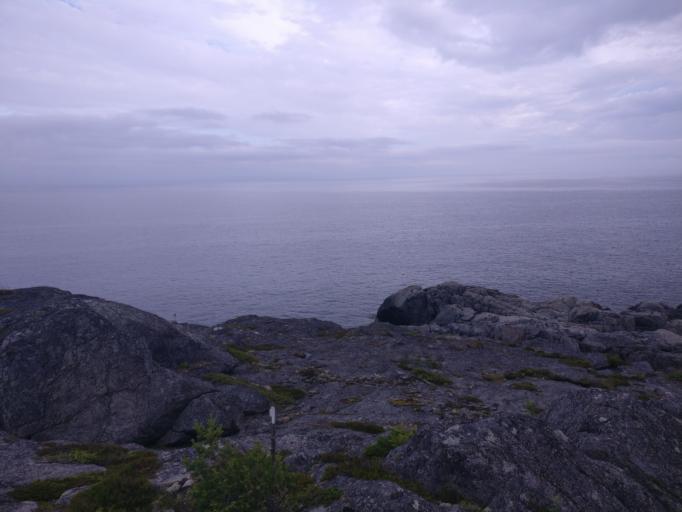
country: SE
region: Vaesternorrland
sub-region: Haernoesands Kommun
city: Haernoesand
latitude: 62.5995
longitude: 18.0548
